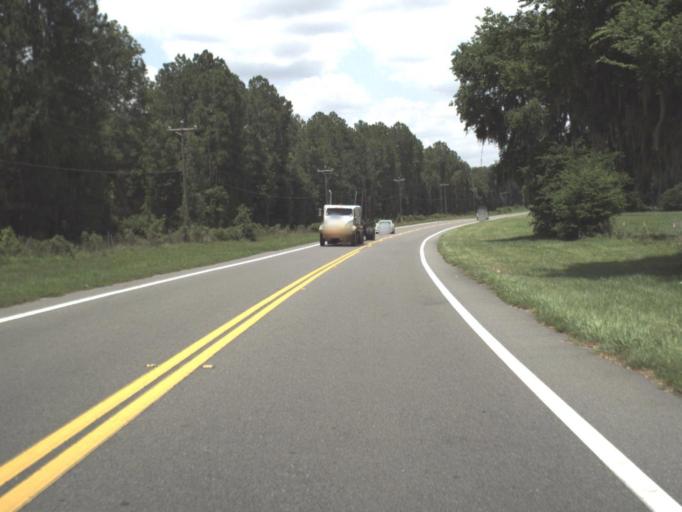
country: US
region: Florida
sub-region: Alachua County
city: Gainesville
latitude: 29.5866
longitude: -82.3913
